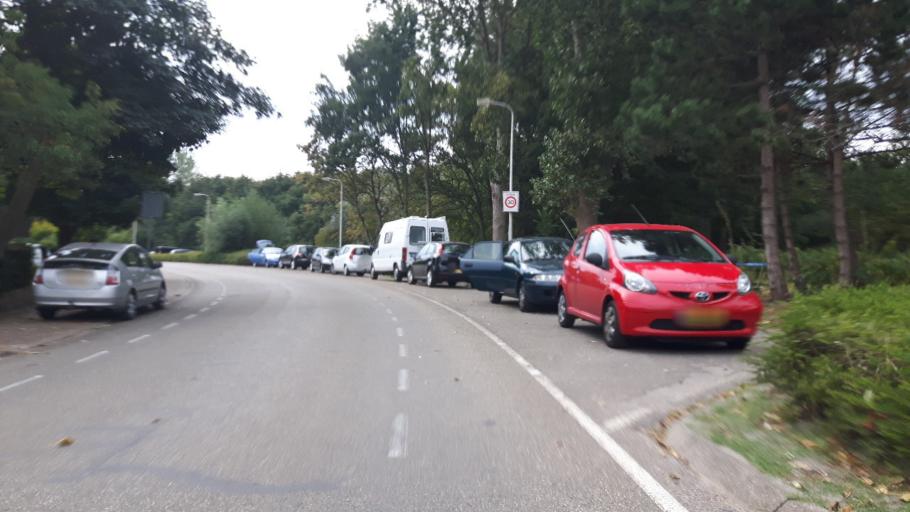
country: NL
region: South Holland
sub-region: Gemeente Hillegom
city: Hillegom
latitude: 52.3036
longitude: 4.5401
